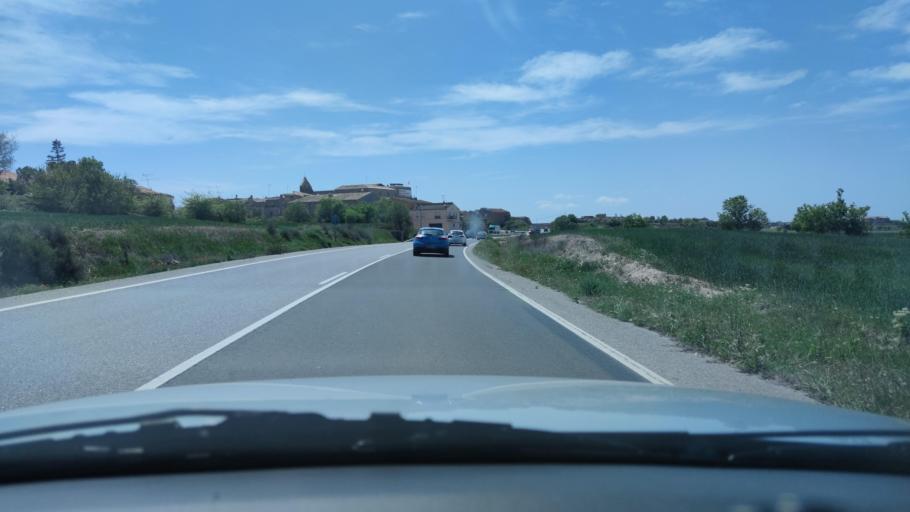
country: ES
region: Catalonia
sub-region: Provincia de Lleida
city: Mont-roig del Camp
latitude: 41.7532
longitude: 1.2373
